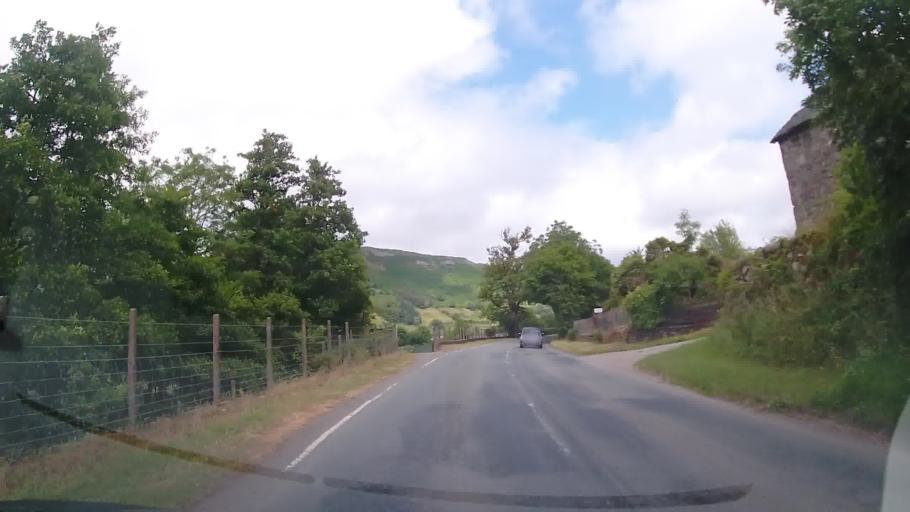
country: GB
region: Wales
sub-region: Sir Powys
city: Llangynog
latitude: 52.8225
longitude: -3.4000
